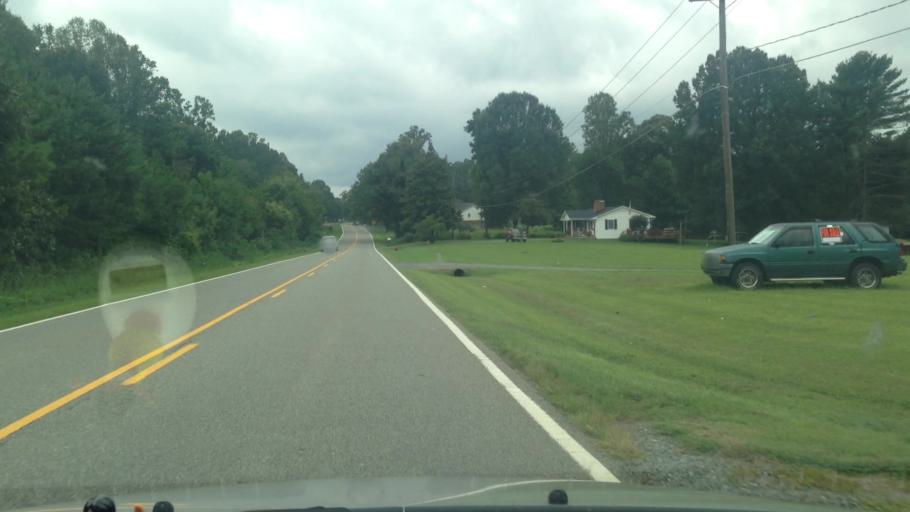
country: US
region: North Carolina
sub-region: Stokes County
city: Walnut Cove
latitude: 36.2638
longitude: -80.1464
